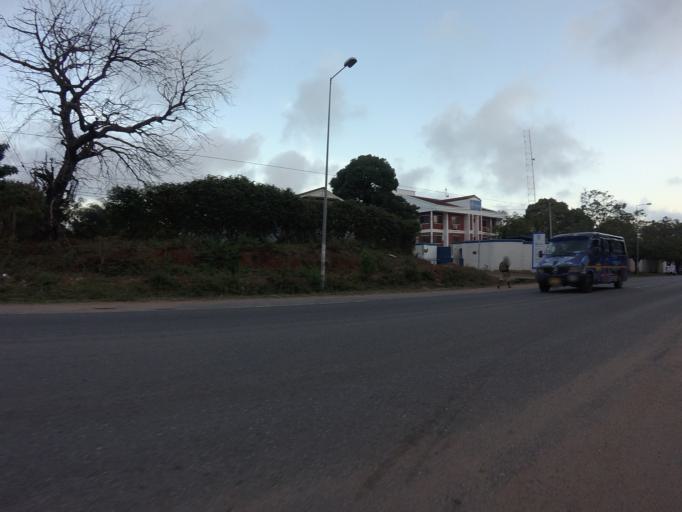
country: GH
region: Greater Accra
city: Accra
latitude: 5.5720
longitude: -0.1842
